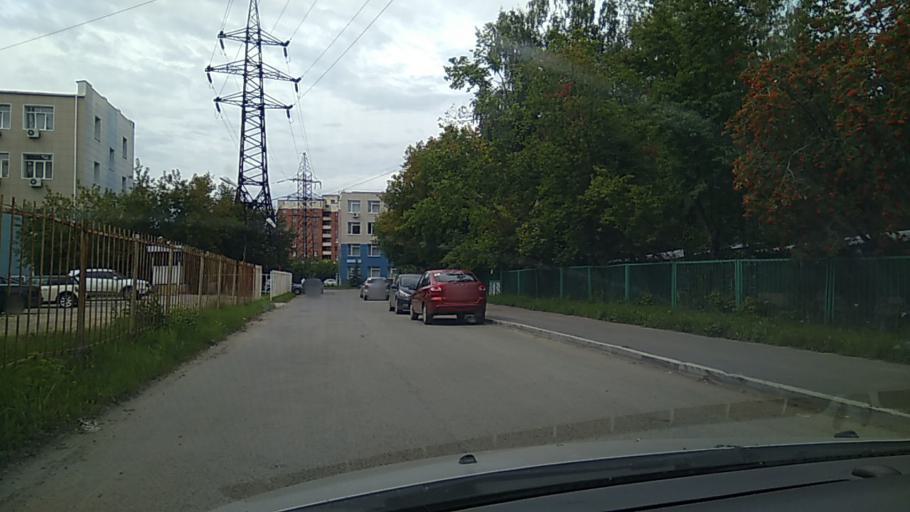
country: RU
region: Sverdlovsk
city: Yekaterinburg
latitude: 56.8822
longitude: 60.6203
